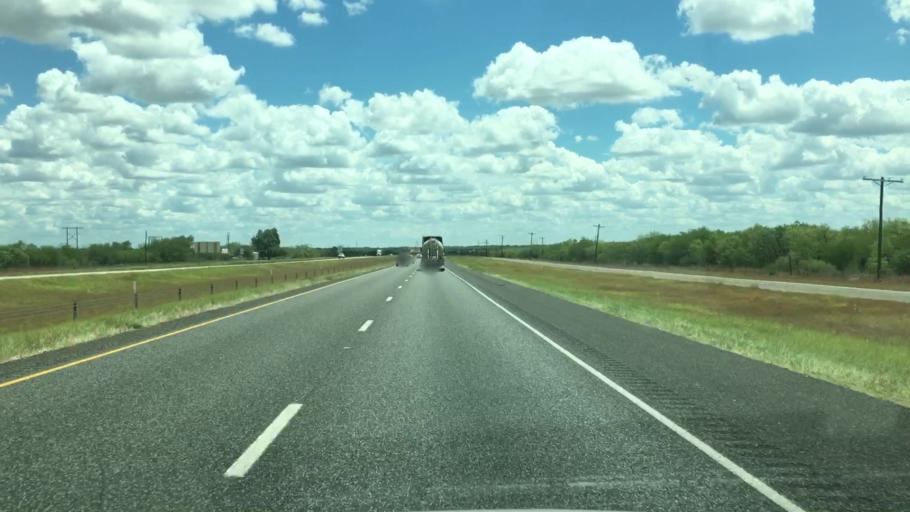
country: US
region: Texas
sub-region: Atascosa County
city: Pleasanton
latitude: 28.8555
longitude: -98.3845
